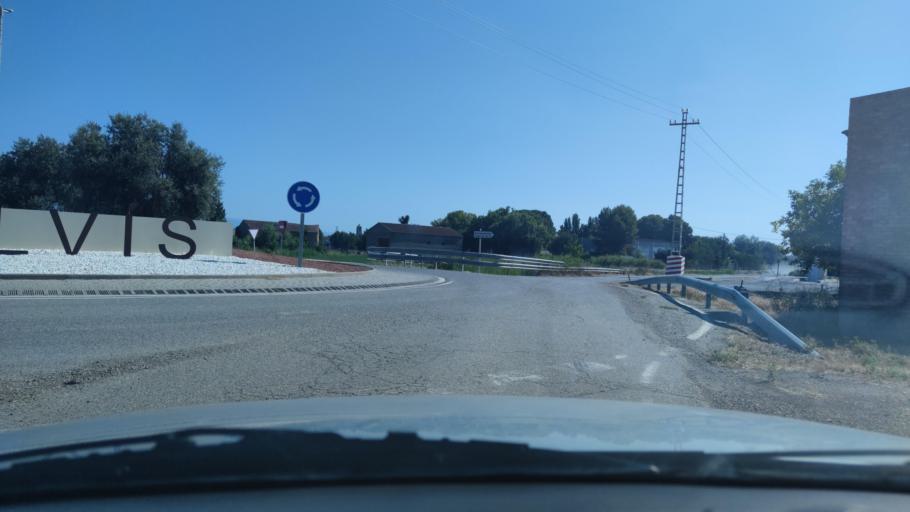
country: ES
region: Catalonia
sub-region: Provincia de Lleida
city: Bellvis
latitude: 41.6660
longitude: 0.8122
